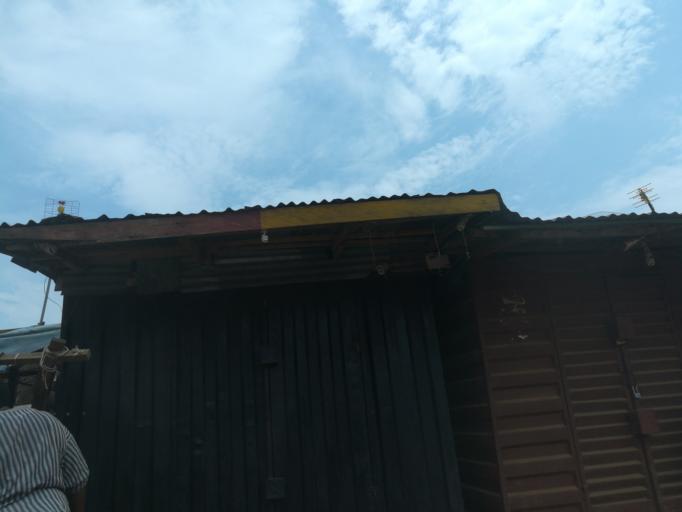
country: NG
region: Lagos
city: Oshodi
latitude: 6.5514
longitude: 3.3249
